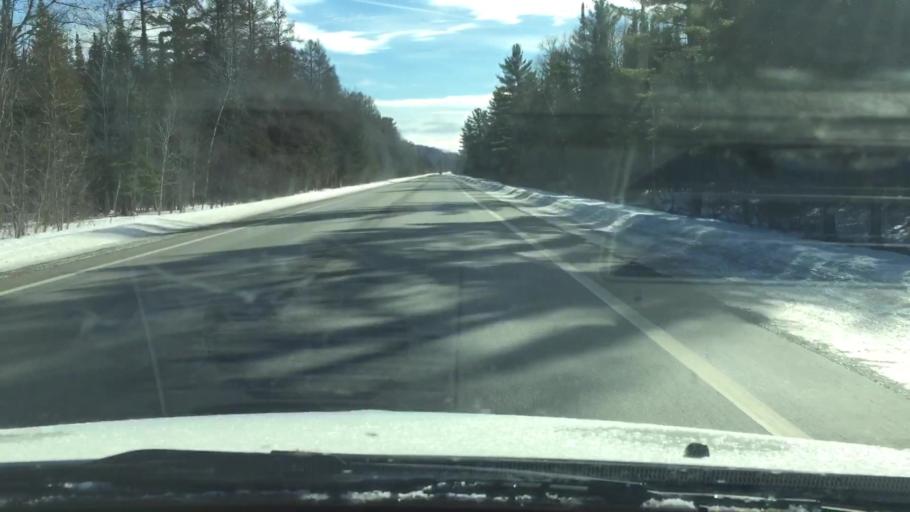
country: US
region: Michigan
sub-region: Antrim County
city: Mancelona
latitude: 45.0261
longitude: -85.0658
